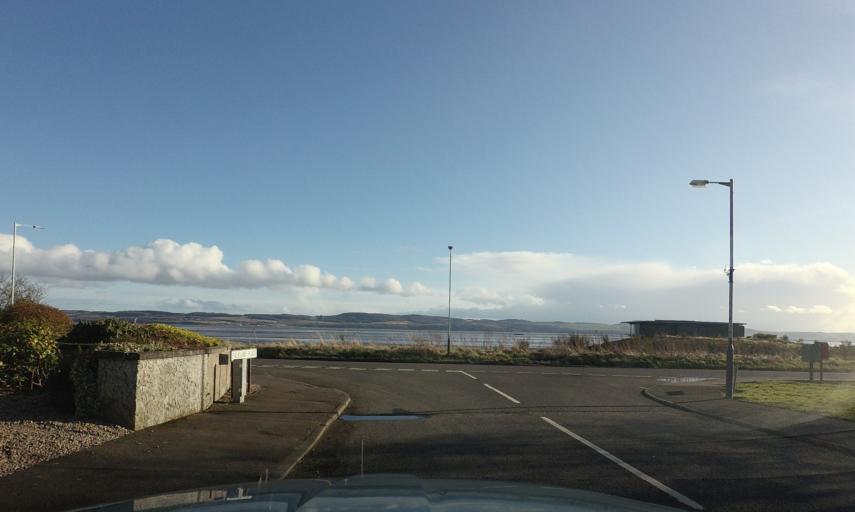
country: GB
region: Scotland
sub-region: Angus
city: Muirhead
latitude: 56.4516
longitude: -3.0731
